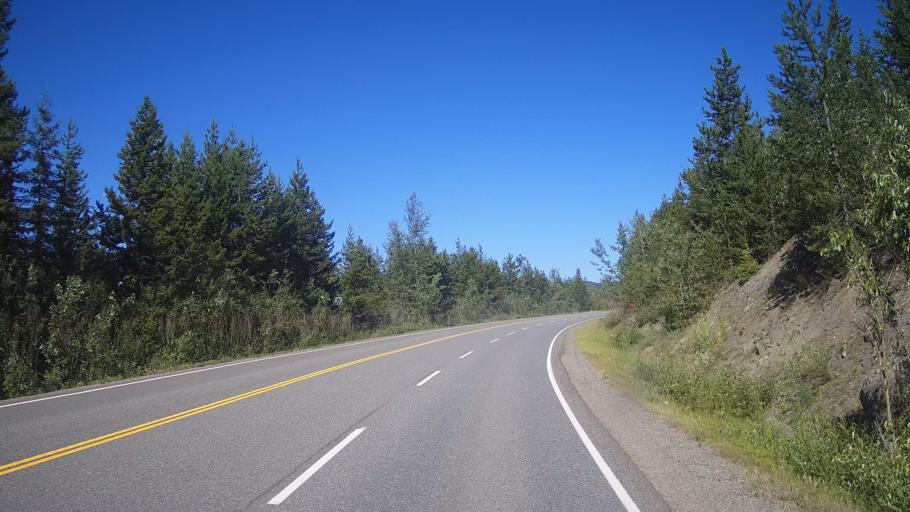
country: CA
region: British Columbia
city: Kamloops
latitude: 51.4942
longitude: -120.3330
